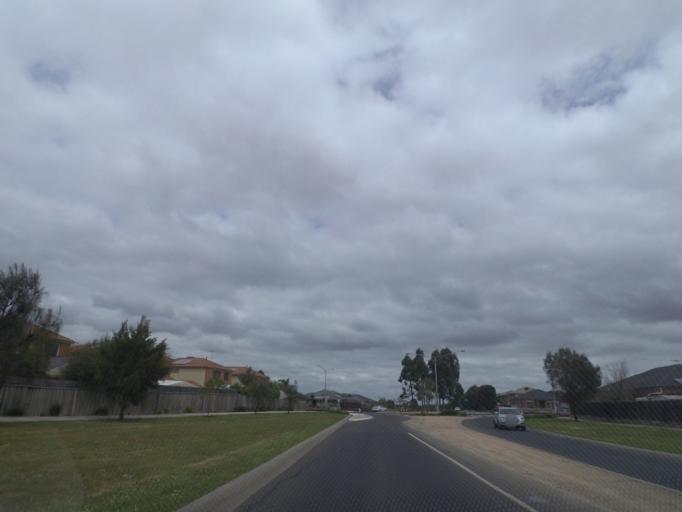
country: AU
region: Victoria
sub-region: Melton
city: Taylors Hill
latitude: -37.7155
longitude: 144.7548
